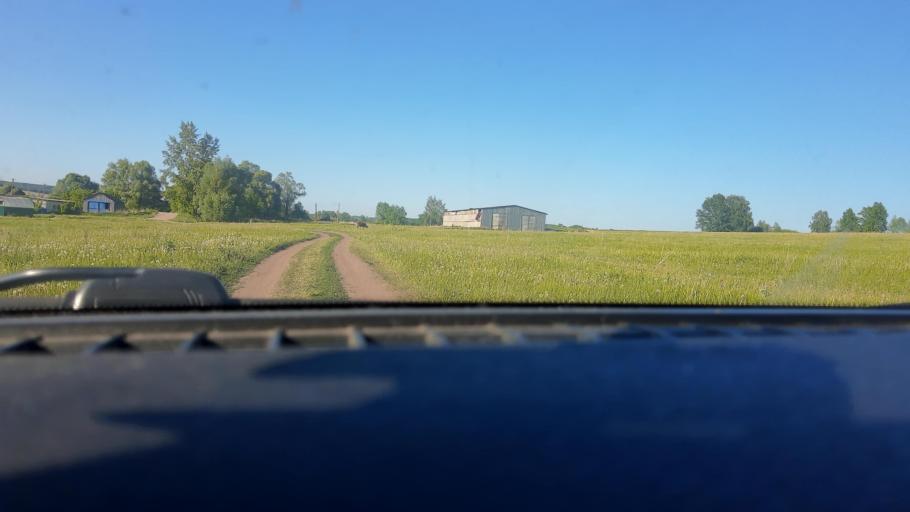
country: RU
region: Bashkortostan
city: Ulukulevo
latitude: 54.5522
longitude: 56.3231
